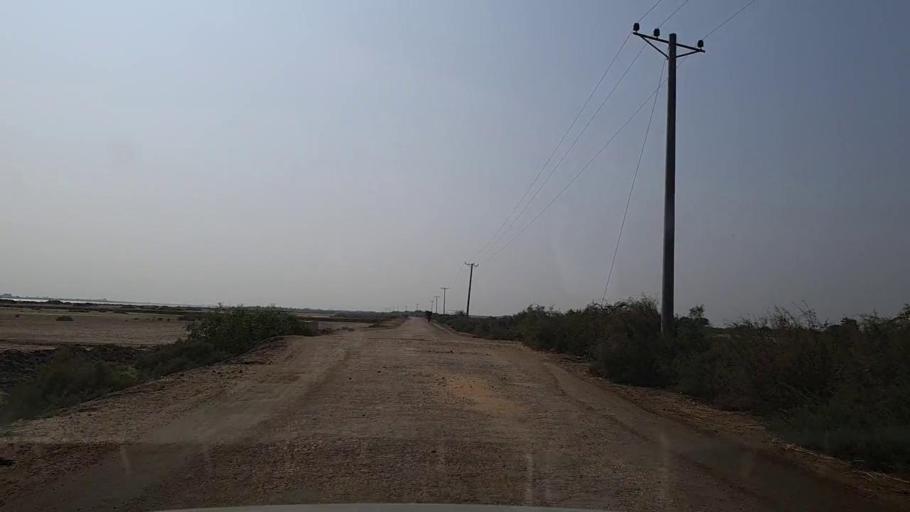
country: PK
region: Sindh
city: Mirpur Sakro
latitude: 24.5404
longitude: 67.6021
